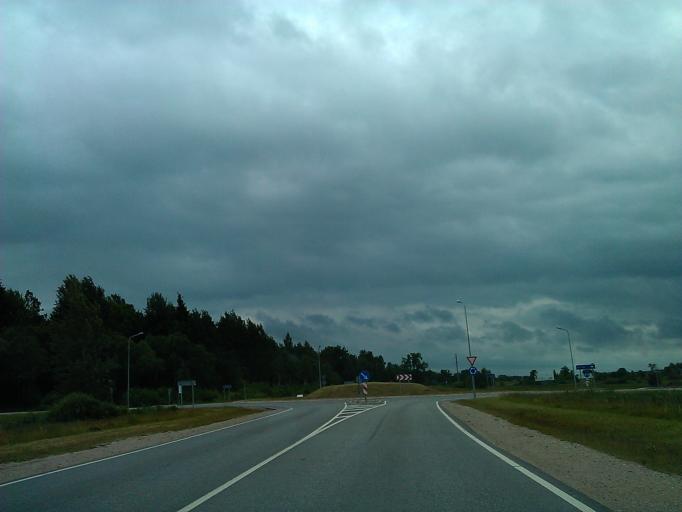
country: LV
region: Kuldigas Rajons
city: Kuldiga
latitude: 56.9728
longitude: 22.0154
